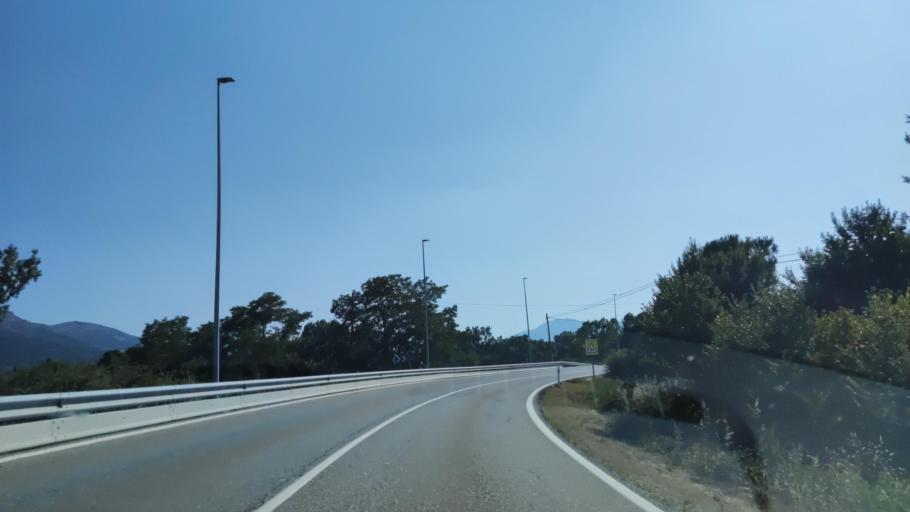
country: ES
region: Madrid
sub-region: Provincia de Madrid
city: Lozoya
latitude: 40.9496
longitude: -3.7882
